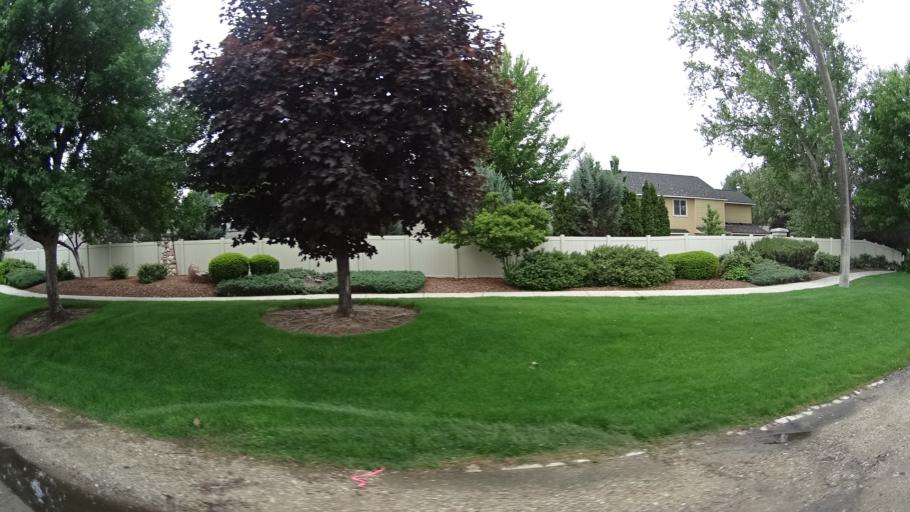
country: US
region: Idaho
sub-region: Ada County
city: Meridian
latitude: 43.6339
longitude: -116.4195
